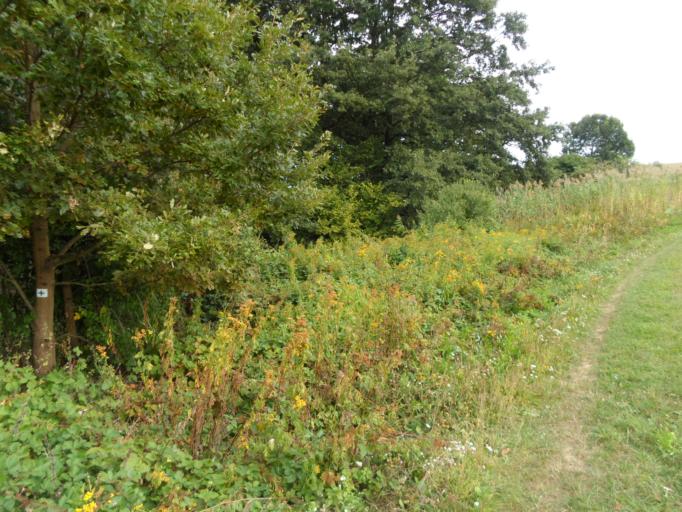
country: HU
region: Veszprem
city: Ajka
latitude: 47.1871
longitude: 17.6132
